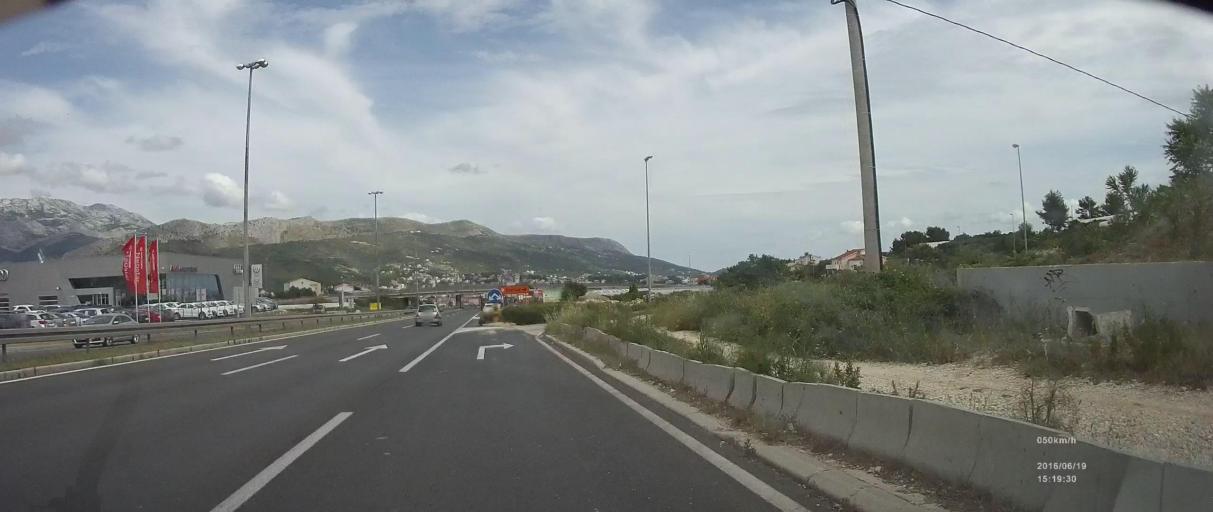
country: HR
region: Splitsko-Dalmatinska
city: Kamen
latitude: 43.5066
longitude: 16.5053
